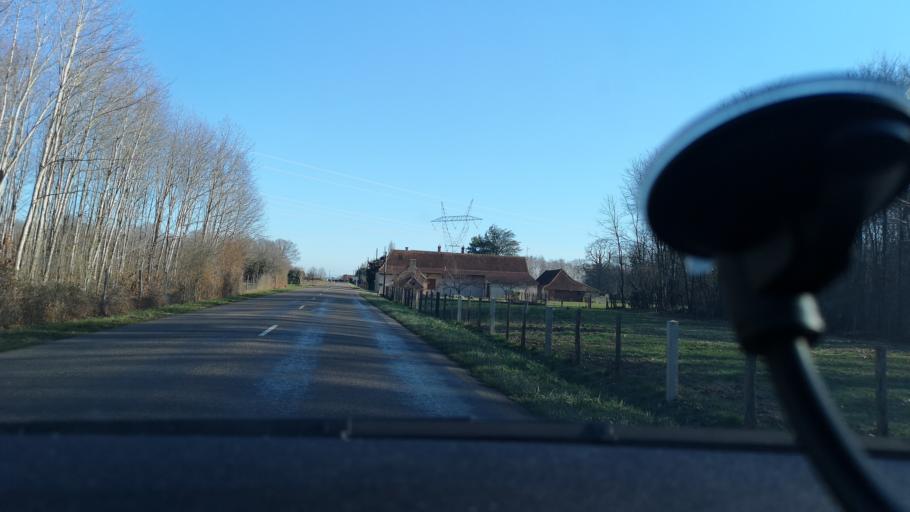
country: FR
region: Bourgogne
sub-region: Departement de Saone-et-Loire
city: Saint-Germain-du-Bois
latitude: 46.7480
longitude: 5.2074
